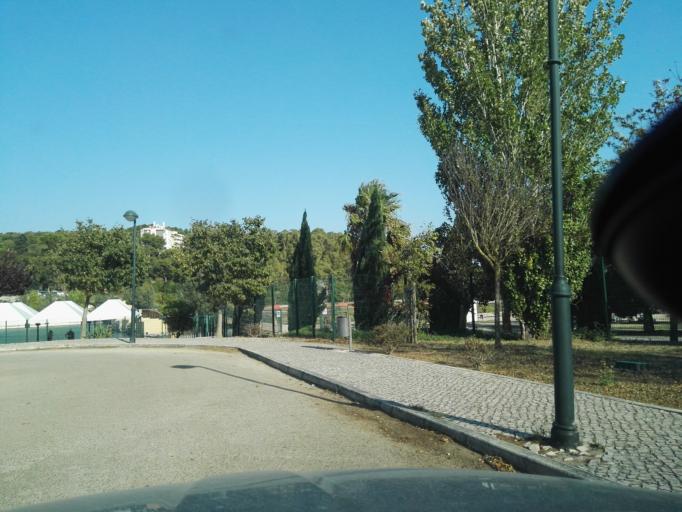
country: PT
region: Lisbon
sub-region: Oeiras
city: Linda-a-Velha
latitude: 38.7044
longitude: -9.2560
